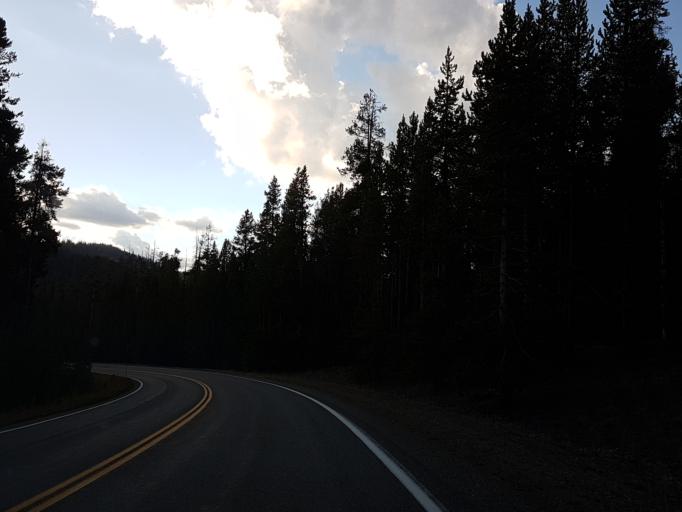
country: US
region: Montana
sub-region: Gallatin County
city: West Yellowstone
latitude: 44.4490
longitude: -110.6943
